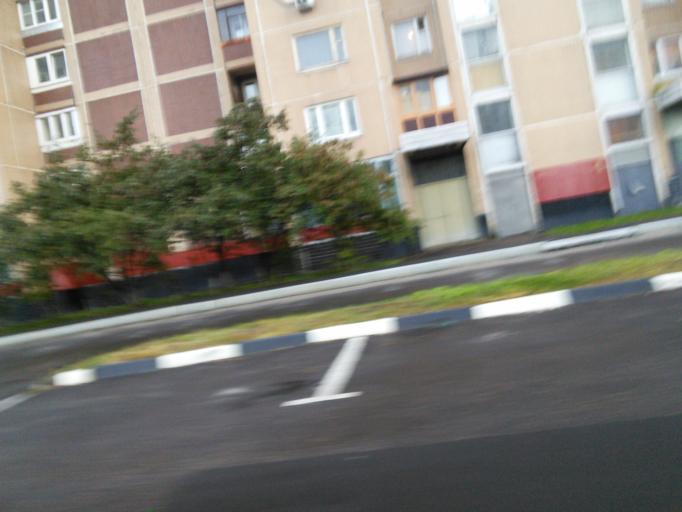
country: RU
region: Moscow
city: Orekhovo-Borisovo Severnoye
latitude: 55.6370
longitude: 37.6715
